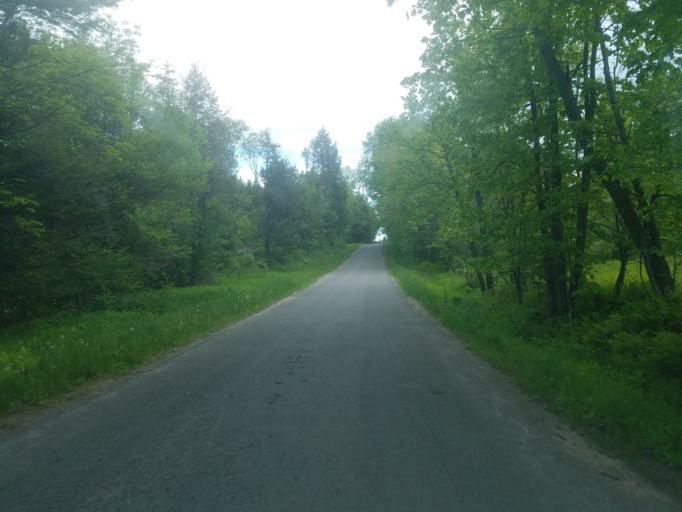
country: US
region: New York
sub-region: Herkimer County
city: Herkimer
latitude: 43.2419
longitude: -74.9775
